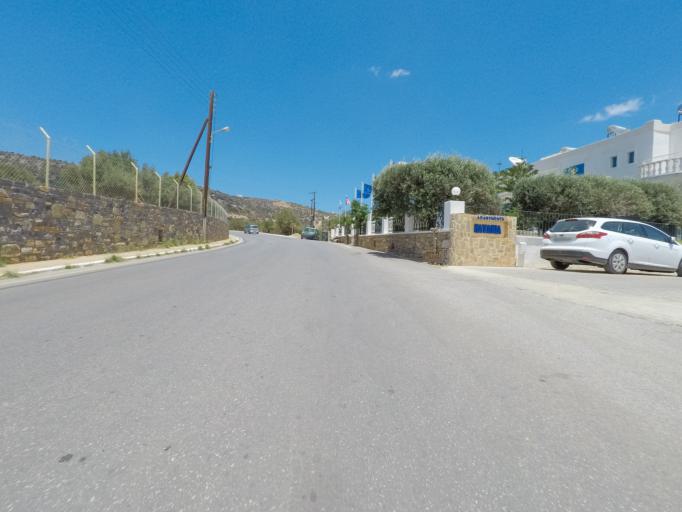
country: GR
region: Crete
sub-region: Nomos Lasithiou
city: Agios Nikolaos
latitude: 35.2154
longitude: 25.7122
